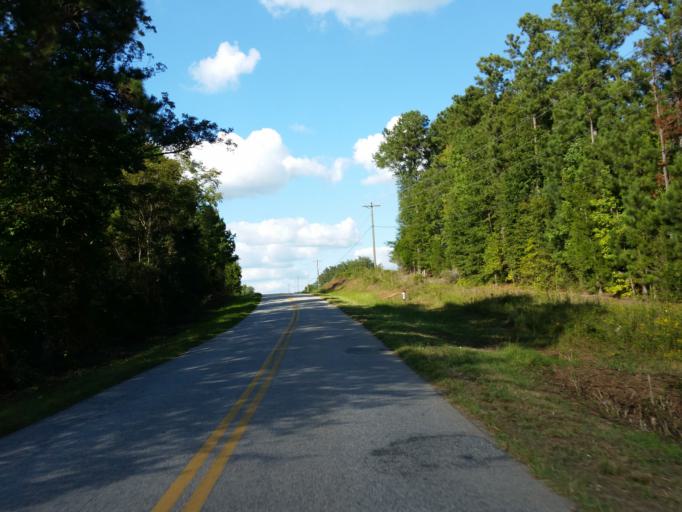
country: US
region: Georgia
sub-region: Butts County
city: Indian Springs
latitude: 33.2072
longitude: -83.9993
